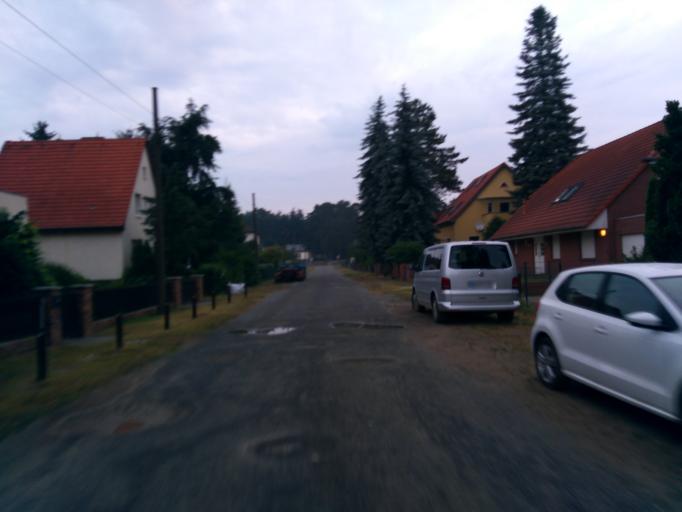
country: DE
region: Brandenburg
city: Falkensee
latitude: 52.5688
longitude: 13.0897
